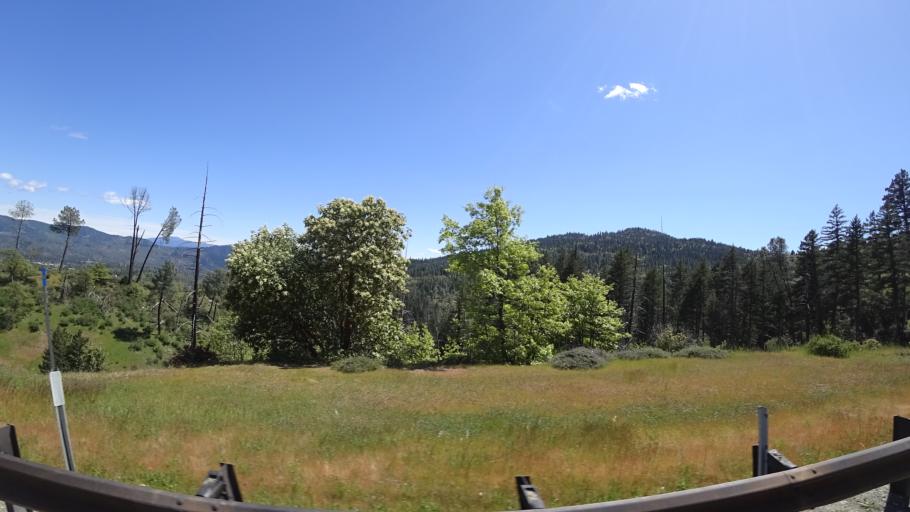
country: US
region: California
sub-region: Trinity County
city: Weaverville
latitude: 40.7416
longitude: -122.9784
